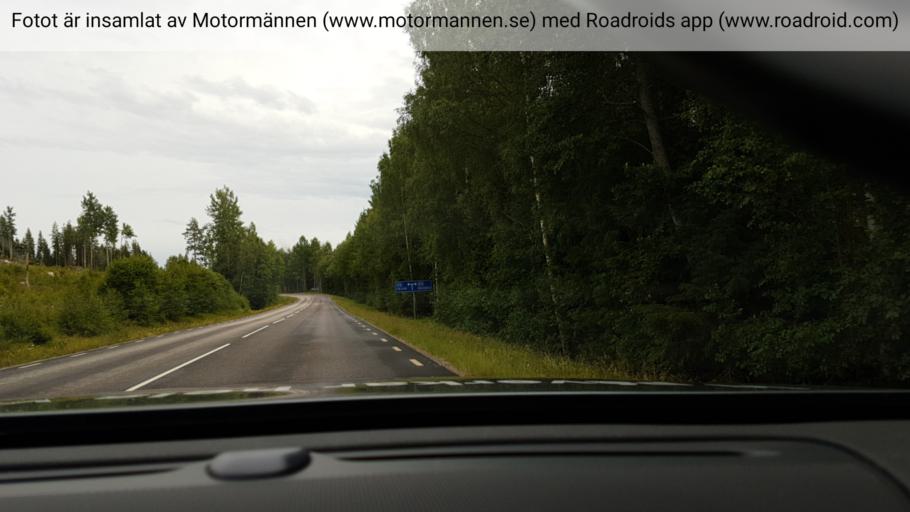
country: SE
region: Dalarna
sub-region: Ludvika Kommun
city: Ludvika
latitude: 60.2904
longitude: 15.2503
